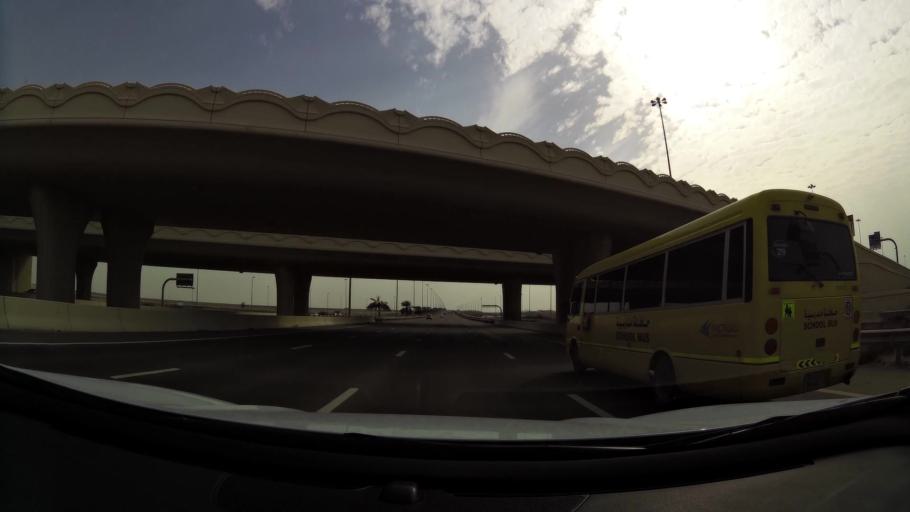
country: AE
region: Abu Dhabi
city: Abu Dhabi
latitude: 24.4097
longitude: 54.6729
